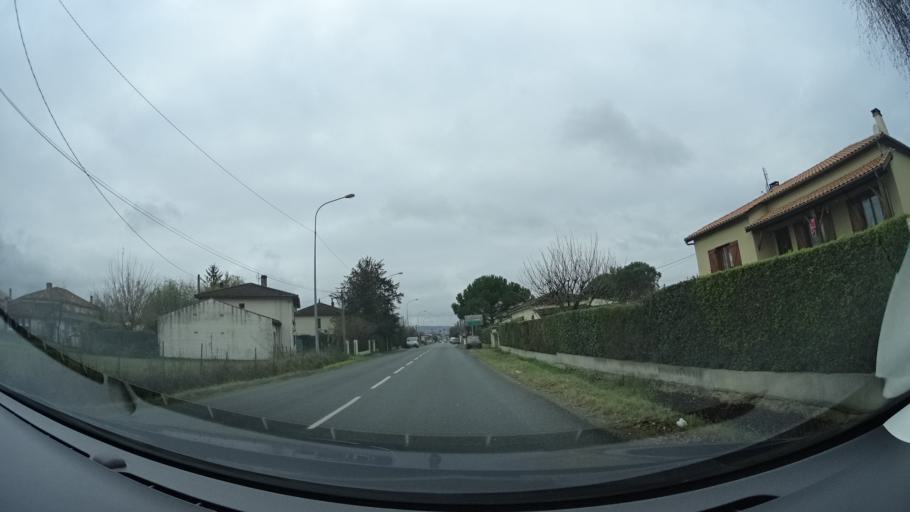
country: FR
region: Aquitaine
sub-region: Departement du Lot-et-Garonne
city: Villeneuve-sur-Lot
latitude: 44.4217
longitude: 0.7218
